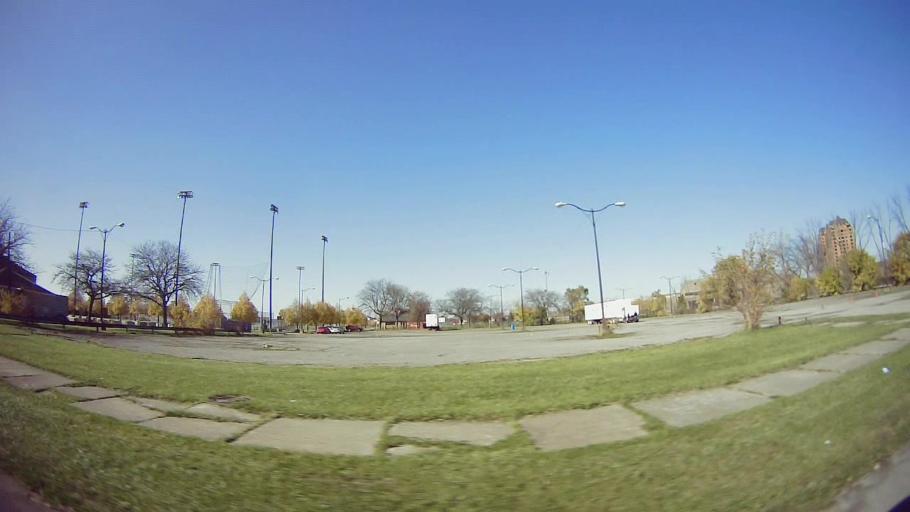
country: US
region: Michigan
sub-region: Wayne County
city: Highland Park
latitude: 42.3555
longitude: -83.1011
